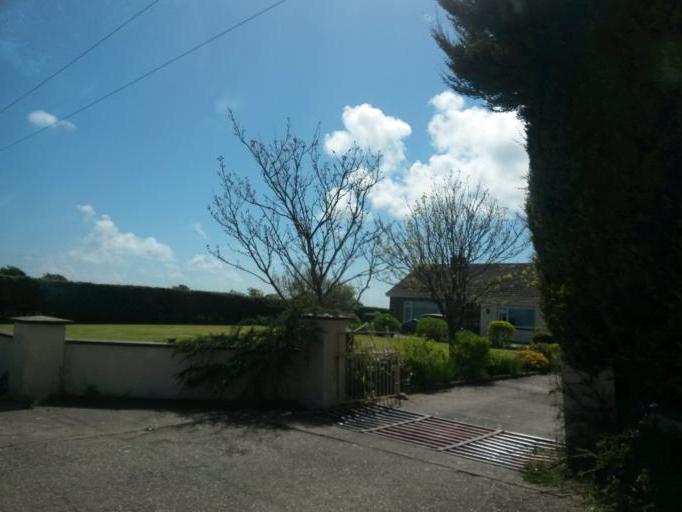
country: IE
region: Munster
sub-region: Waterford
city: Dunmore East
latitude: 52.1875
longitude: -6.8944
